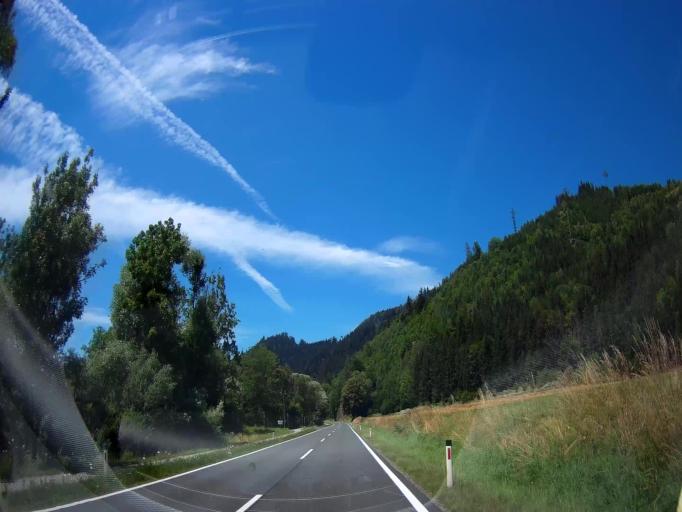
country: AT
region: Carinthia
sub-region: Politischer Bezirk Sankt Veit an der Glan
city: Micheldorf
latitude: 46.9026
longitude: 14.4089
